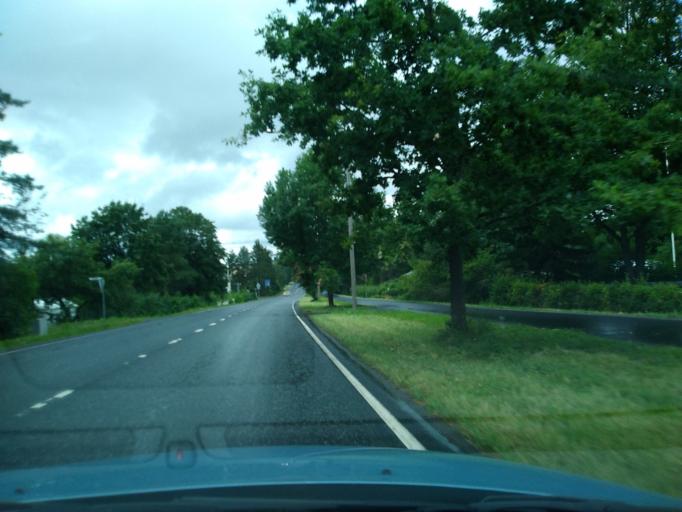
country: FI
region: Haeme
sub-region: Forssa
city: Tammela
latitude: 60.8070
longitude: 23.7763
